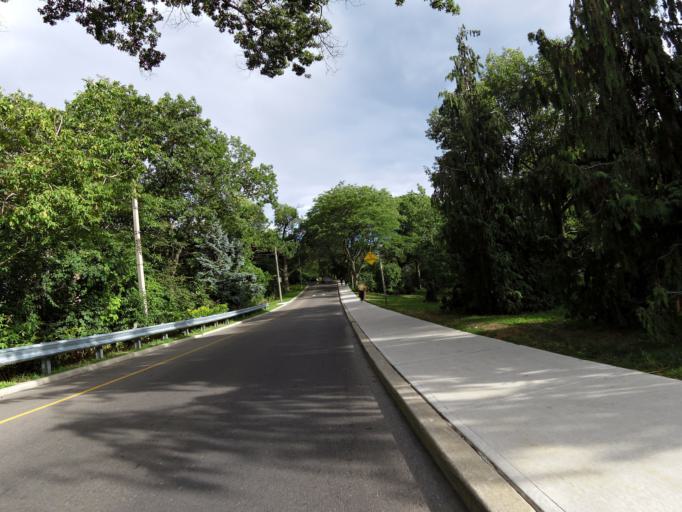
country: CA
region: Ontario
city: Toronto
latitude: 43.6429
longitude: -79.4638
